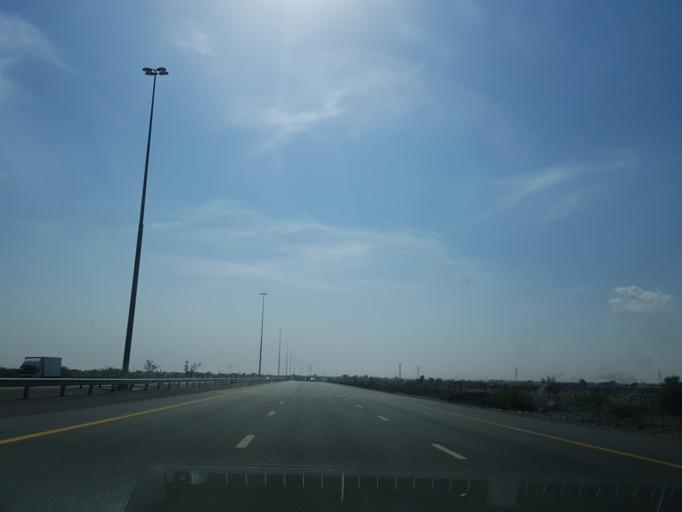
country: AE
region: Ra's al Khaymah
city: Ras al-Khaimah
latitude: 25.7074
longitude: 55.9979
